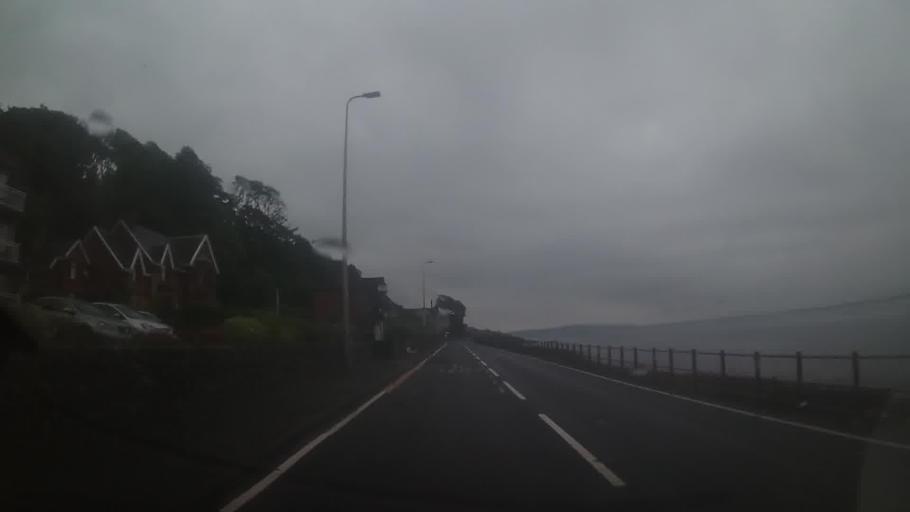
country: GB
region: Scotland
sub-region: North Ayrshire
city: Skelmorlie
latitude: 55.8613
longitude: -4.8898
